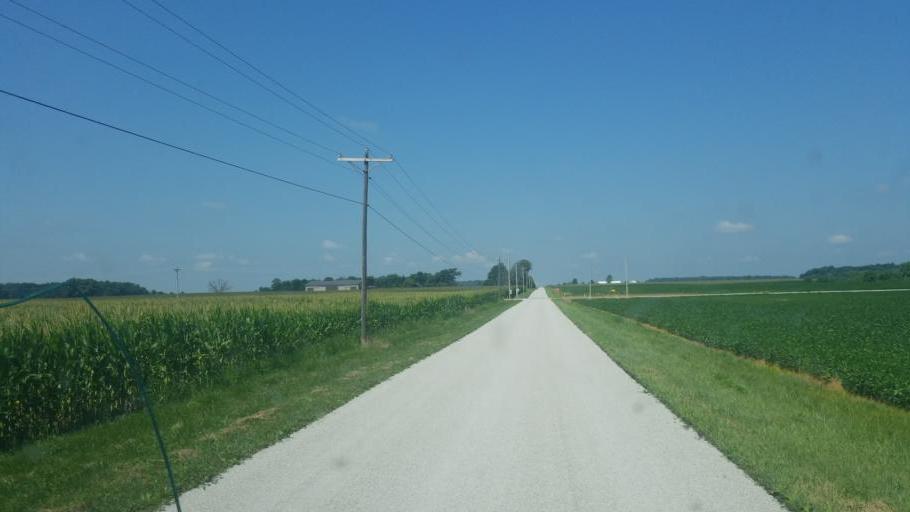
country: US
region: Ohio
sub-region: Hardin County
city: Kenton
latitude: 40.7032
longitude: -83.6709
